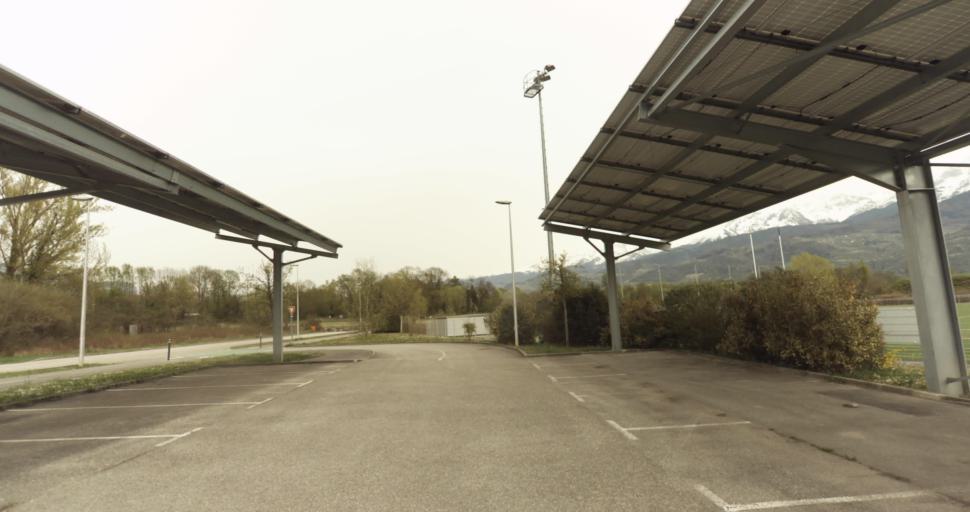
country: FR
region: Rhone-Alpes
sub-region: Departement de l'Isere
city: Montbonnot-Saint-Martin
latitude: 45.2265
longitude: 5.8194
